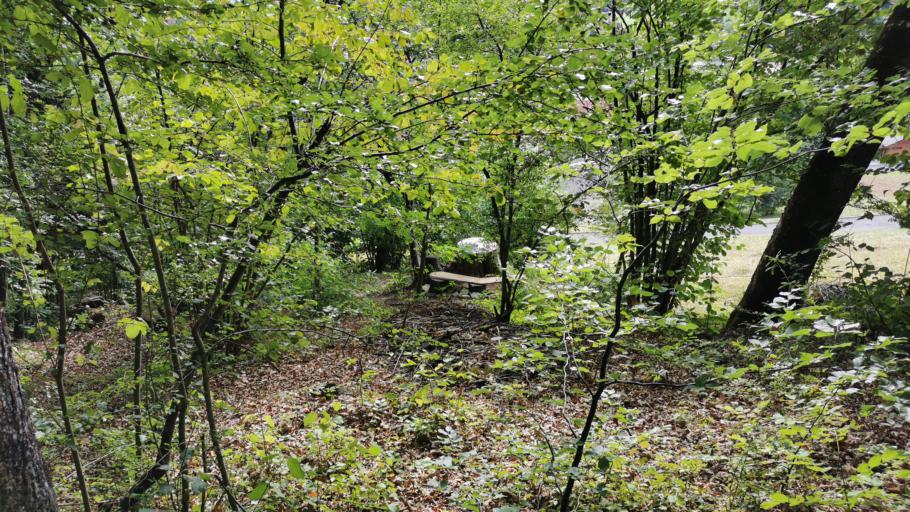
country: FR
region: Rhone-Alpes
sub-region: Departement de la Haute-Savoie
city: Sevrier
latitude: 45.8729
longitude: 6.1376
